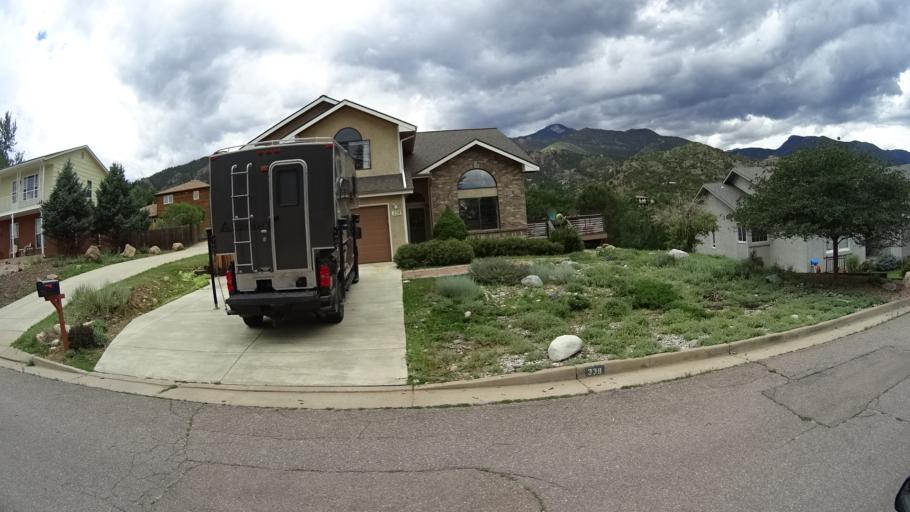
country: US
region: Colorado
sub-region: El Paso County
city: Manitou Springs
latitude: 38.8460
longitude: -104.8946
